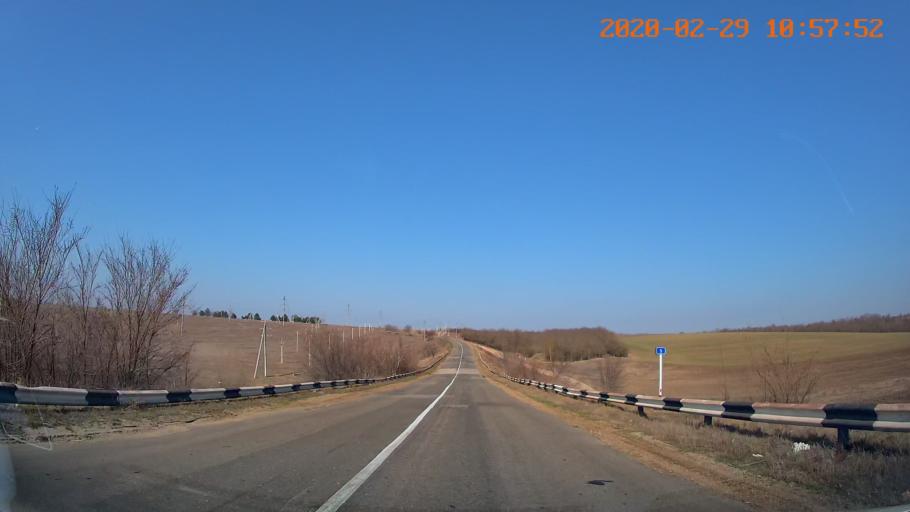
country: MD
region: Telenesti
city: Grigoriopol
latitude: 47.1642
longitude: 29.3195
